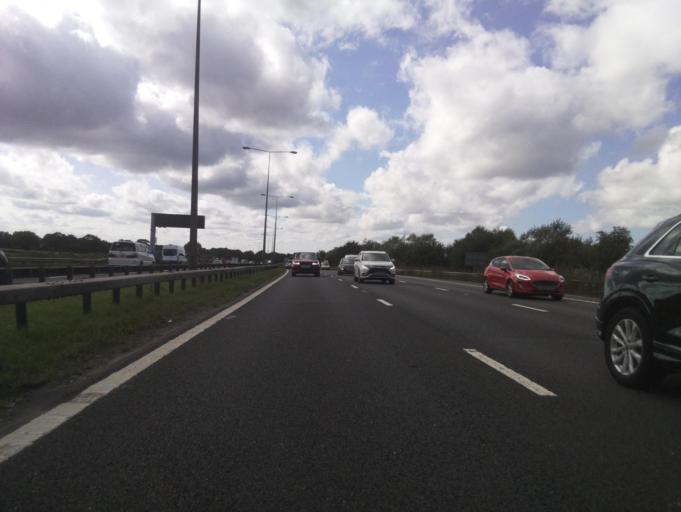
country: GB
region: England
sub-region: Lancashire
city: Clayton-le-Woods
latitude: 53.7099
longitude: -2.6696
